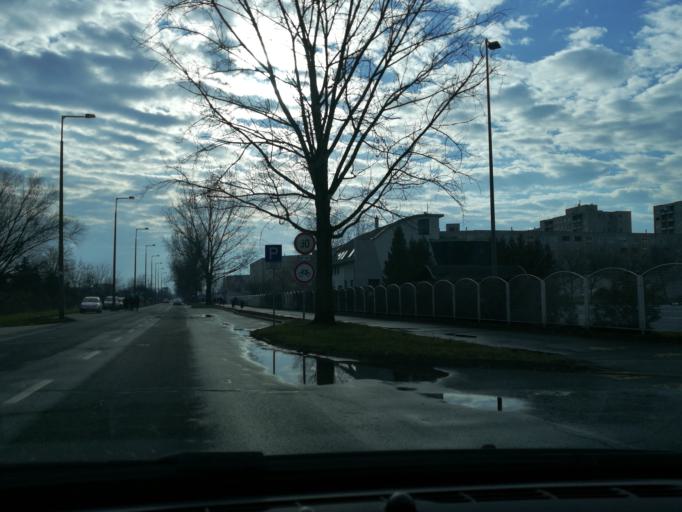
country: HU
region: Szabolcs-Szatmar-Bereg
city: Nyiregyhaza
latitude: 47.9615
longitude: 21.7440
